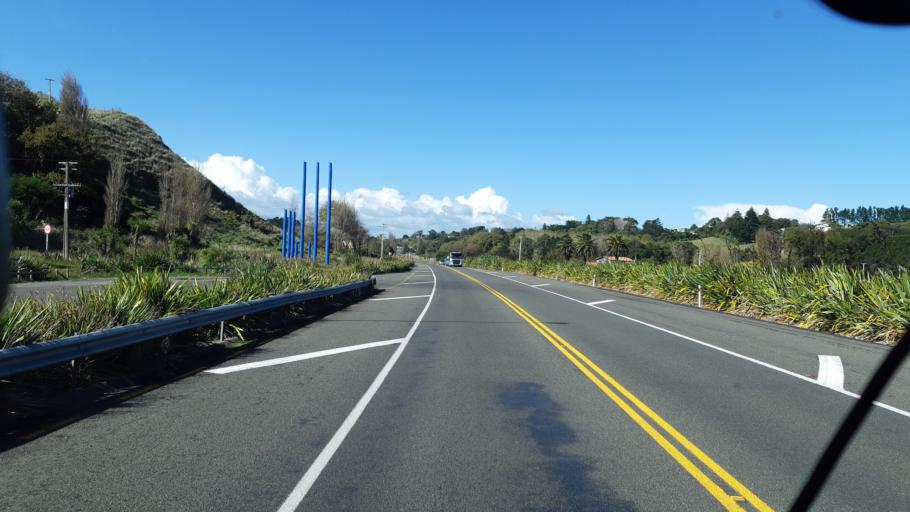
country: NZ
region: Manawatu-Wanganui
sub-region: Wanganui District
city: Wanganui
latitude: -39.9500
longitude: 175.0538
